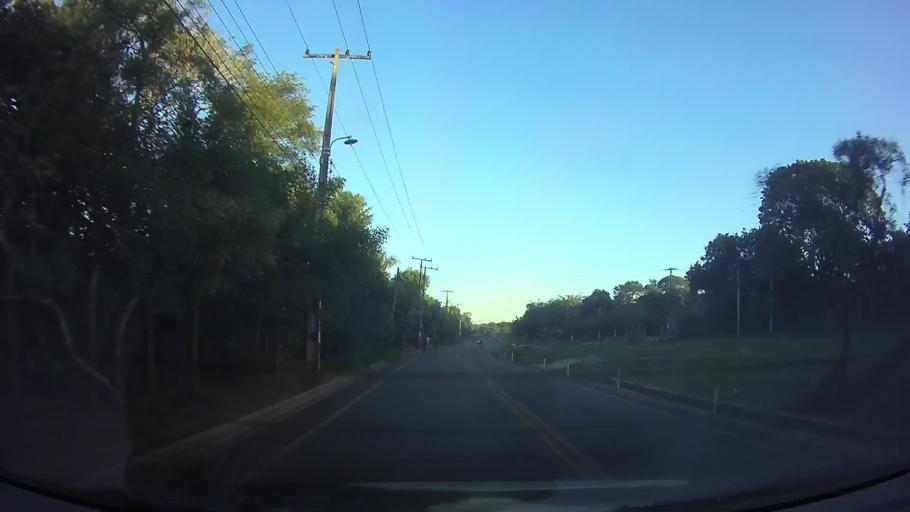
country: PY
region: Central
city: Aregua
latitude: -25.2555
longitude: -57.4566
